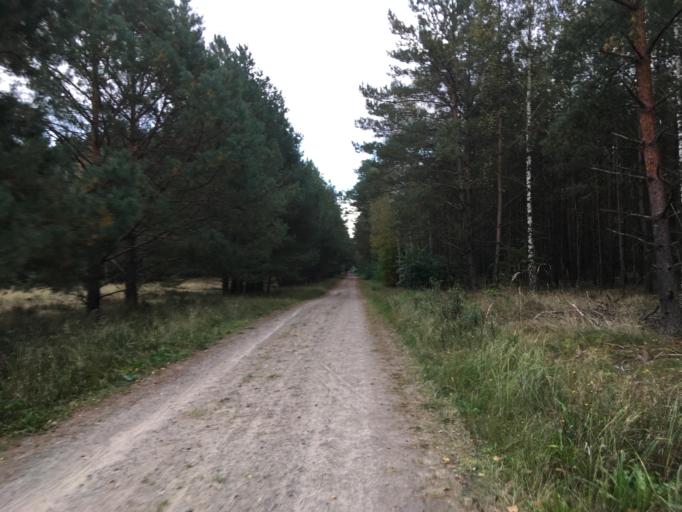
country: DE
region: Brandenburg
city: Birkenwerder
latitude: 52.7065
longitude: 13.3468
